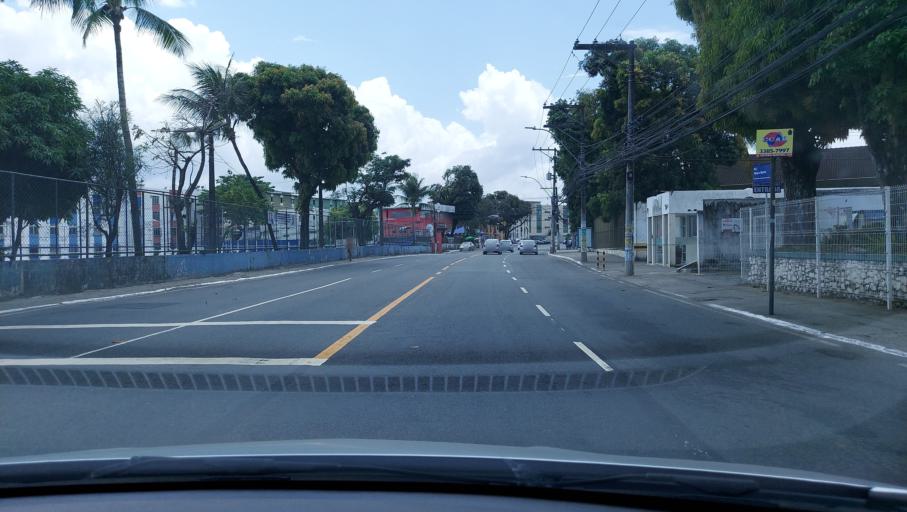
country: BR
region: Bahia
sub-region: Salvador
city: Salvador
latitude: -12.9628
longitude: -38.4717
